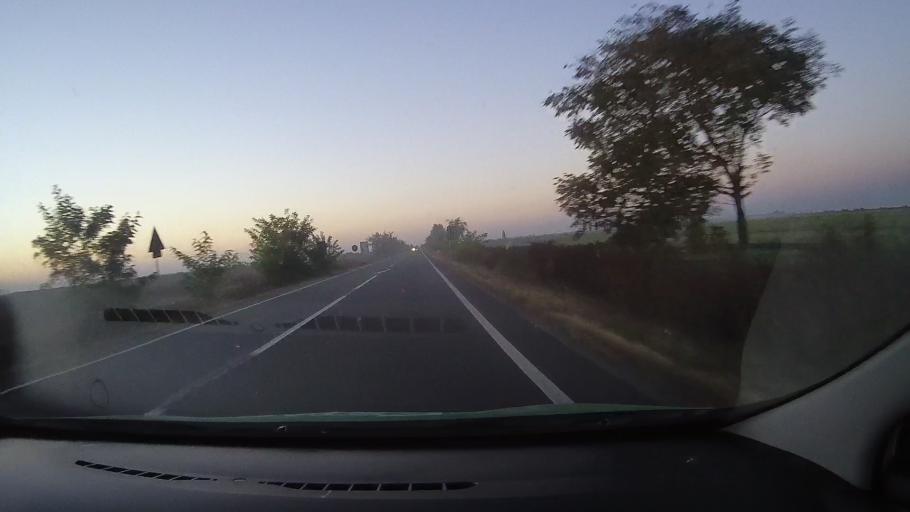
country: RO
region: Bihor
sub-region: Comuna Valea lui Mihai
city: Valea lui Mihai
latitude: 47.4816
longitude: 22.1620
